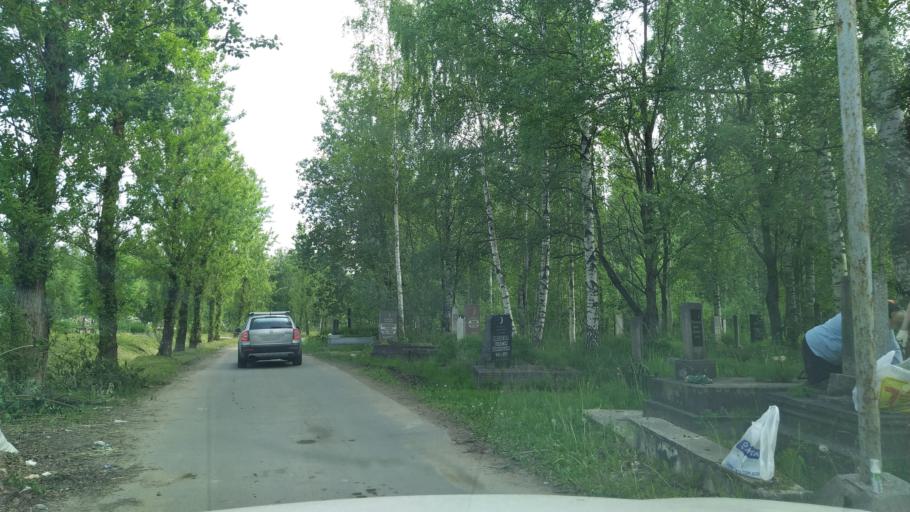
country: RU
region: St.-Petersburg
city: Dachnoye
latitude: 59.7709
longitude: 30.2654
